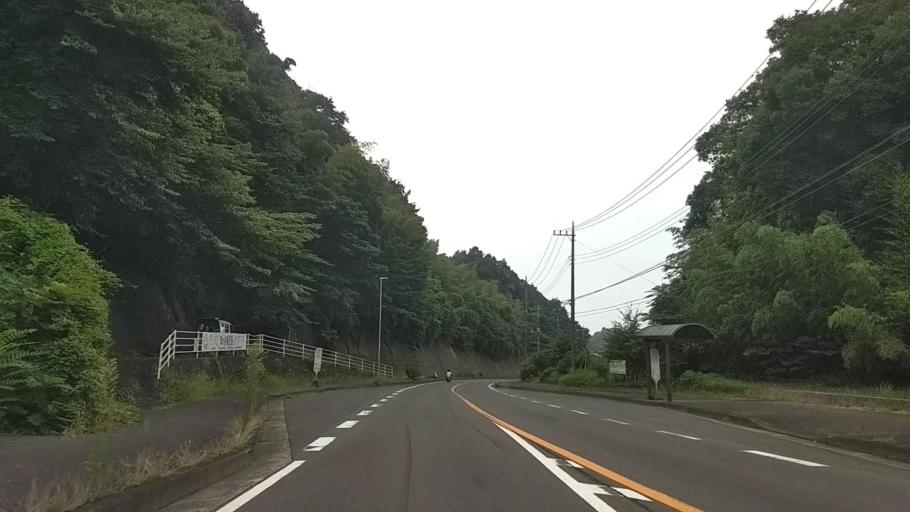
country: JP
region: Kanagawa
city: Hadano
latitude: 35.3345
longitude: 139.2198
